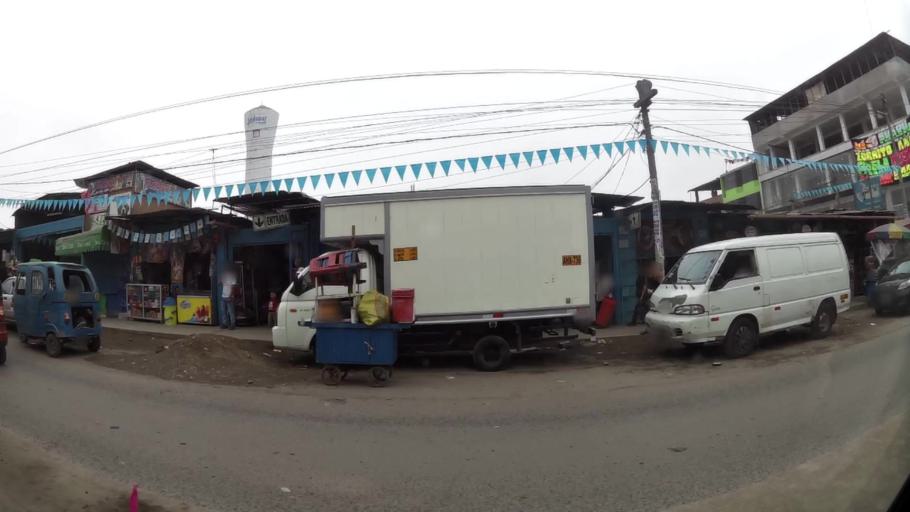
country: PE
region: Lima
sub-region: Lima
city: Surco
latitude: -12.2050
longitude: -76.9417
